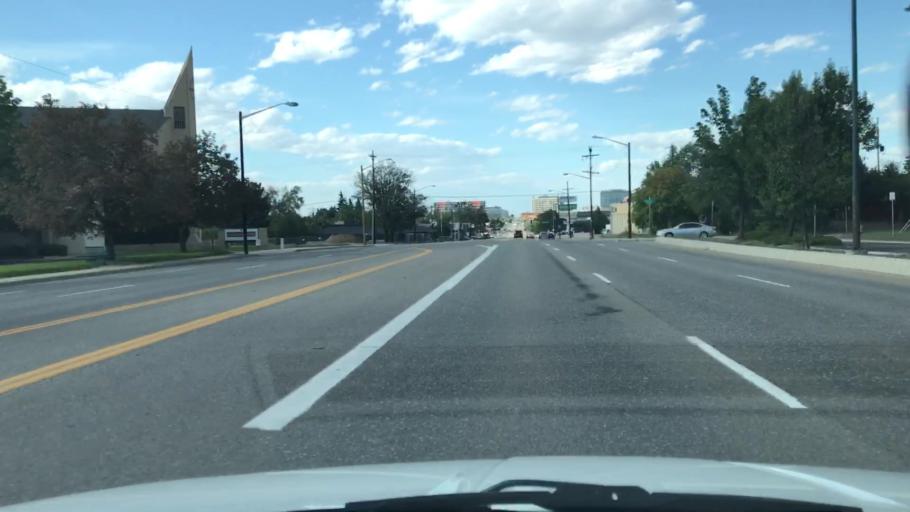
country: US
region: Colorado
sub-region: Arapahoe County
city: Cherry Hills Village
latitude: 39.6629
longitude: -104.9406
